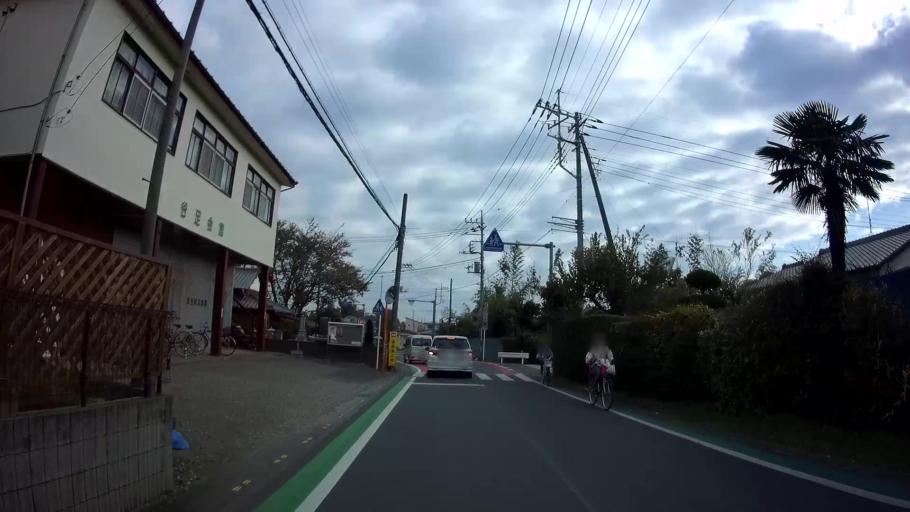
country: JP
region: Saitama
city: Konosu
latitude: 36.0290
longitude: 139.5160
